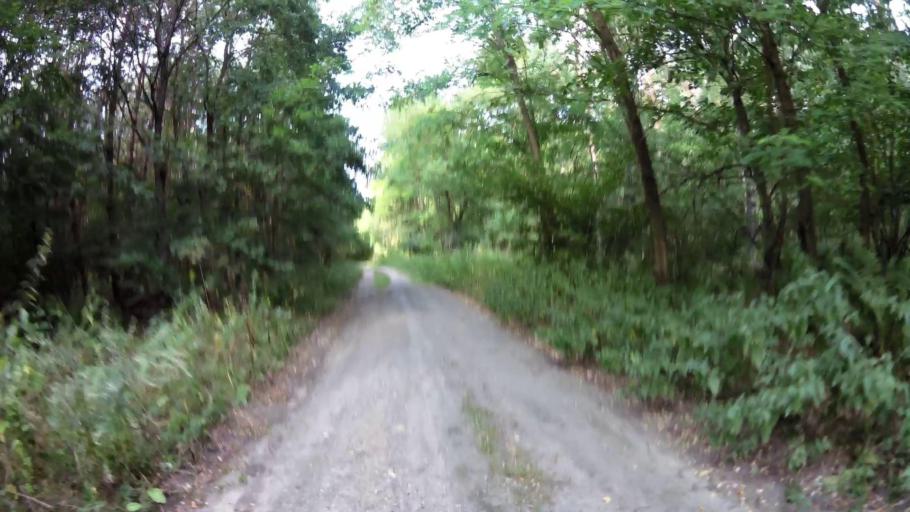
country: PL
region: West Pomeranian Voivodeship
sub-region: Powiat gryfinski
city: Moryn
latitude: 52.8737
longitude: 14.4286
